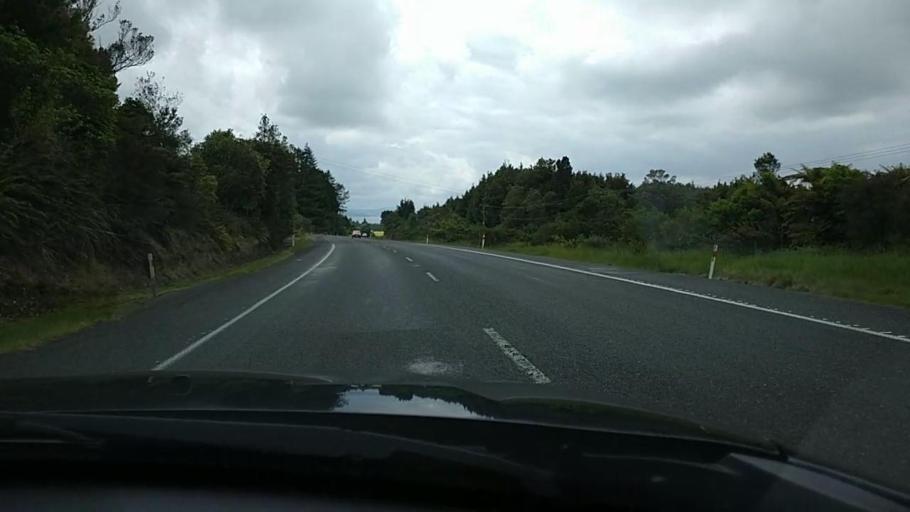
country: NZ
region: Bay of Plenty
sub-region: Rotorua District
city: Rotorua
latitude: -38.0718
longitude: 176.1292
